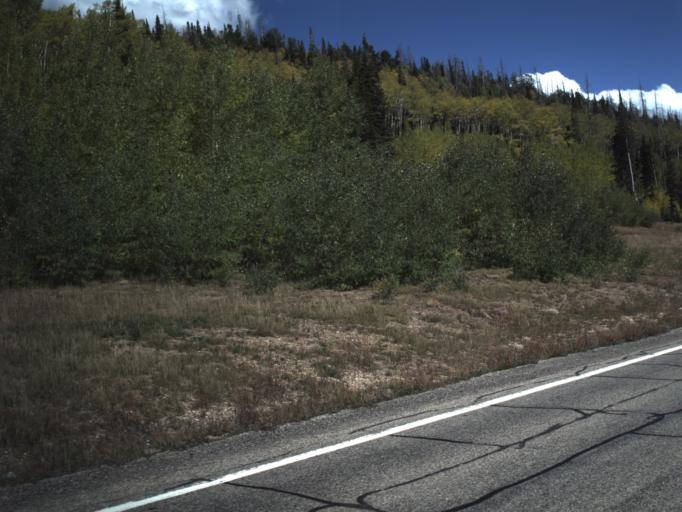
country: US
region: Utah
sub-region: Iron County
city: Cedar City
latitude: 37.5726
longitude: -112.8211
